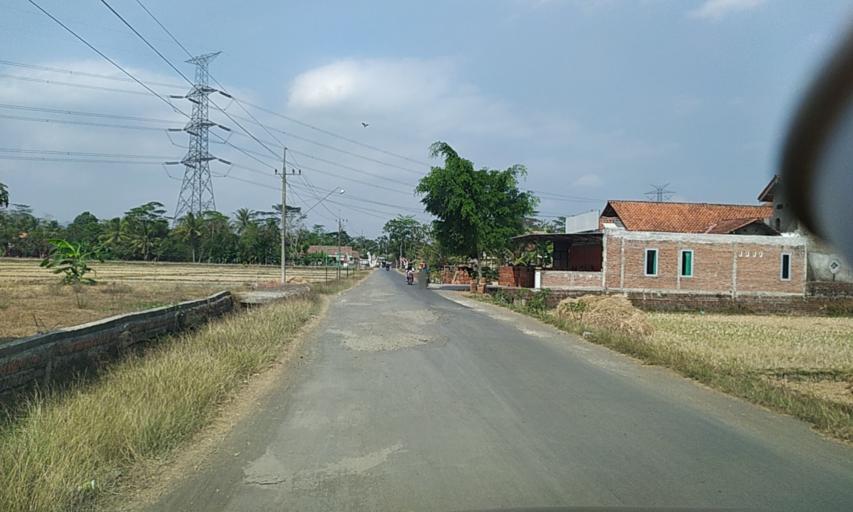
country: ID
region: Central Java
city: Kemantren Satu
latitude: -7.5246
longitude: 108.8657
